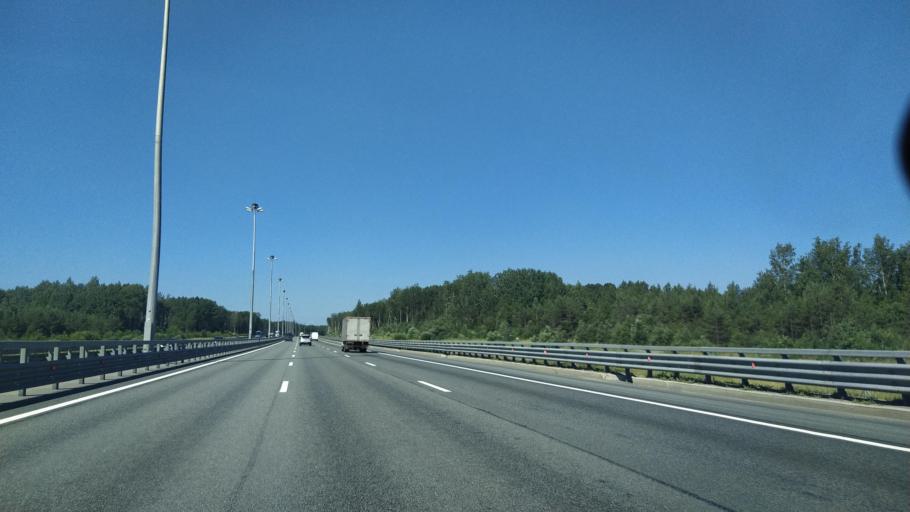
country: RU
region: Leningrad
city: Ol'gino
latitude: 59.8131
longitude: 29.8734
